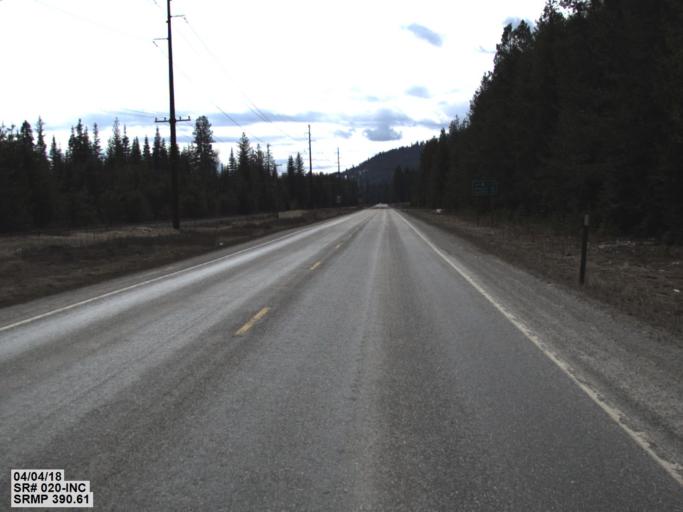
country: CA
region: British Columbia
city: Fruitvale
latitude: 48.6824
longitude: -117.4040
